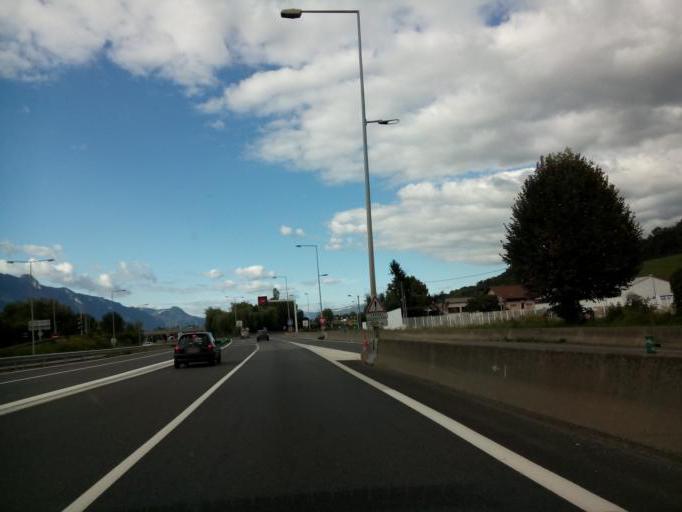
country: FR
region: Rhone-Alpes
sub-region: Departement de la Savoie
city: La Motte-Servolex
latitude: 45.6001
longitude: 5.8928
